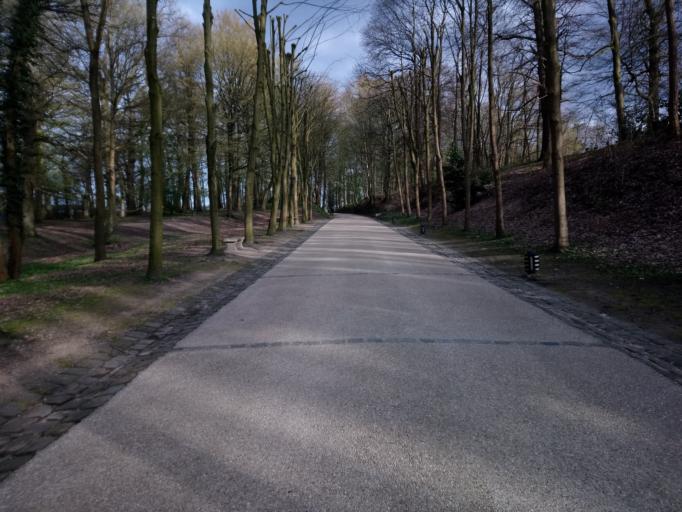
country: FR
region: Ile-de-France
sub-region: Departement du Val-d'Oise
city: Ecouen
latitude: 49.0157
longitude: 2.3801
